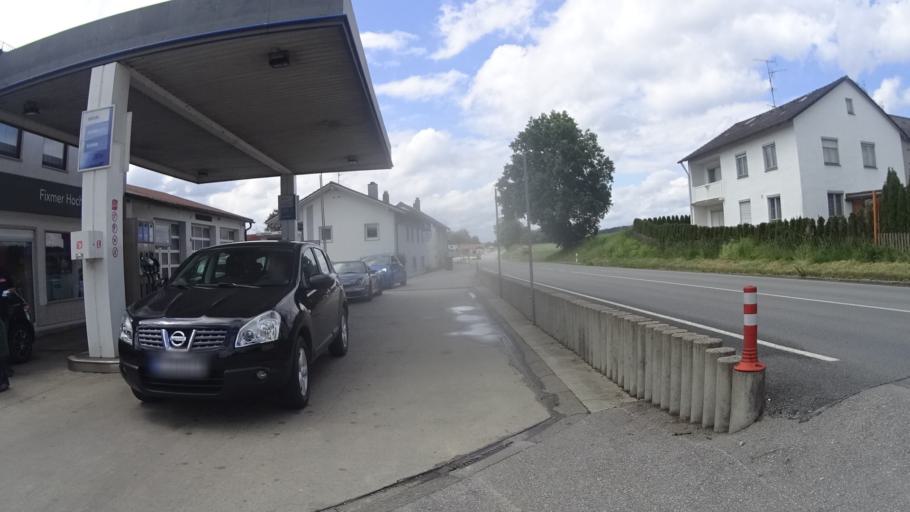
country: DE
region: Bavaria
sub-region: Lower Bavaria
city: Massing
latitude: 48.3964
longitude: 12.6345
